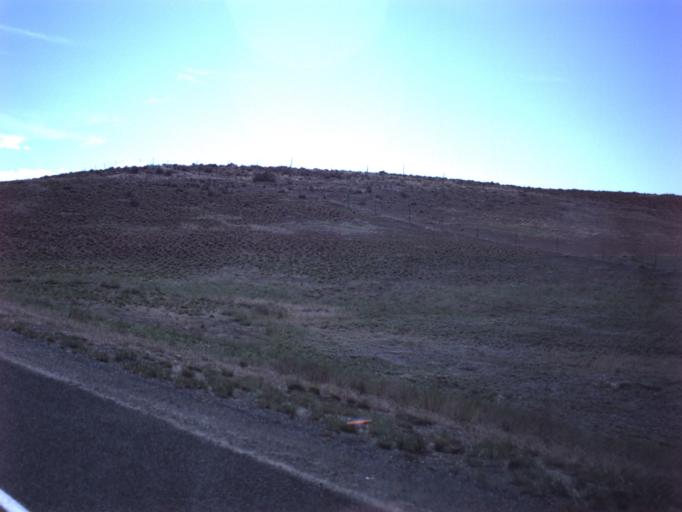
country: US
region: Utah
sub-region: Sanpete County
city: Gunnison
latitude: 39.1702
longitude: -111.8270
